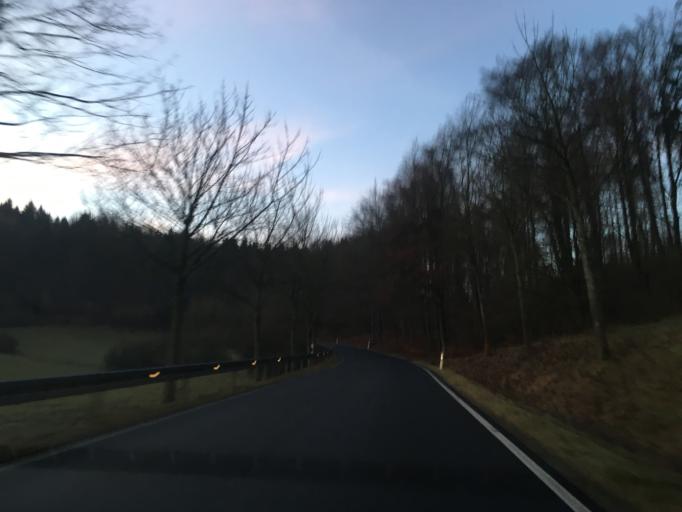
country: DE
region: Thuringia
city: Schleid
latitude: 50.6350
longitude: 9.9274
